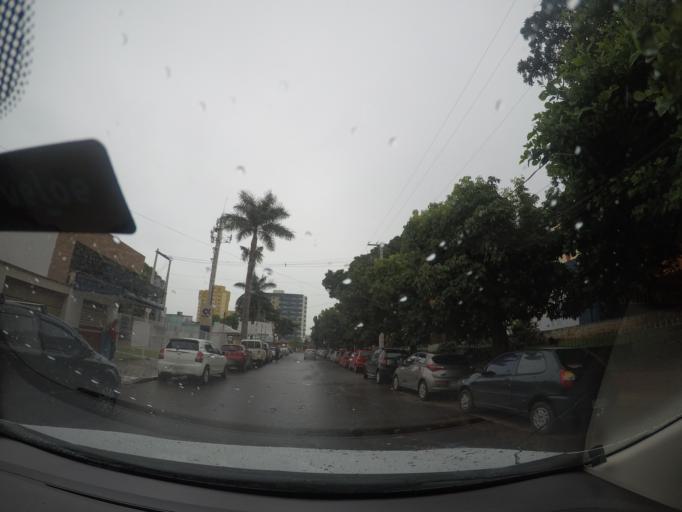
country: BR
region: Goias
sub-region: Goiania
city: Goiania
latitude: -16.6766
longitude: -49.2474
